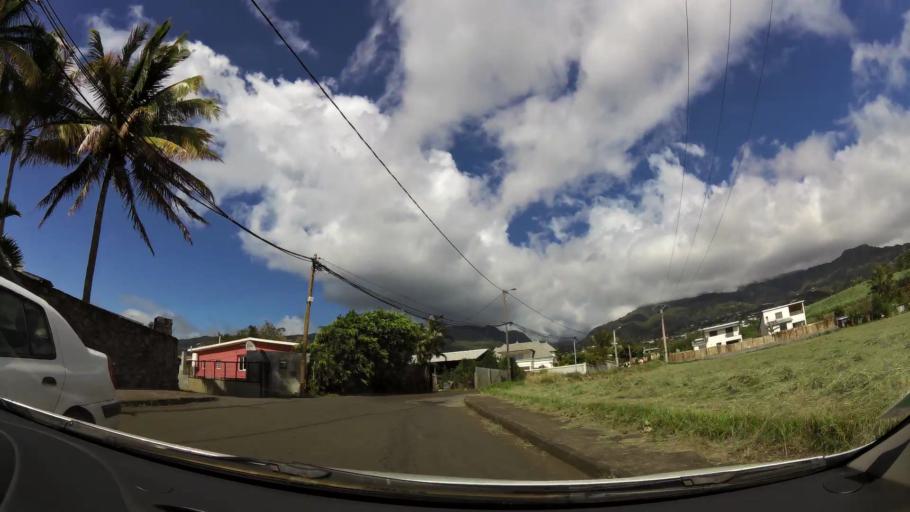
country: RE
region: Reunion
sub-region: Reunion
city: Sainte-Marie
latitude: -20.9198
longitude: 55.5010
